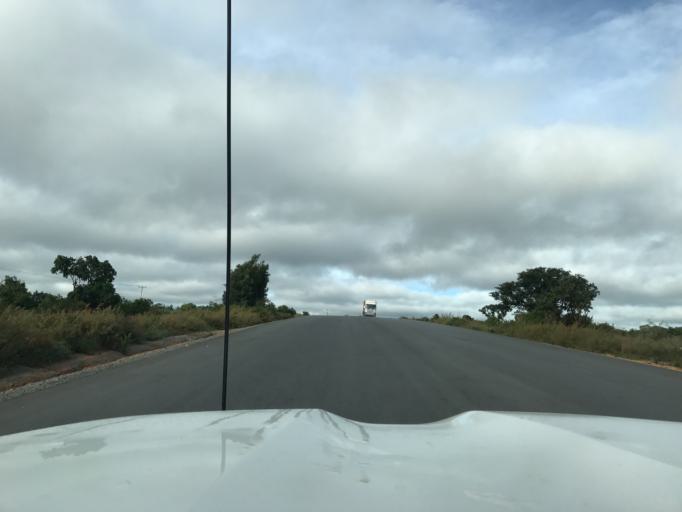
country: TZ
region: Iringa
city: Makungu
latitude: -8.3585
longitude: 35.2363
